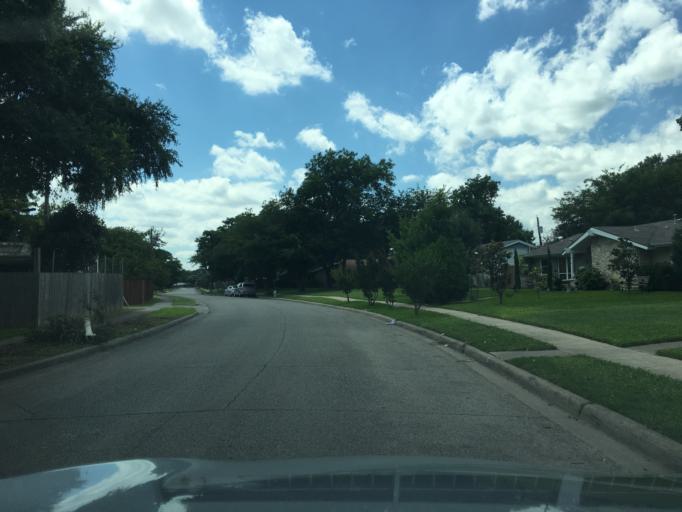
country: US
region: Texas
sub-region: Dallas County
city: Richardson
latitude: 32.9502
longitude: -96.7093
